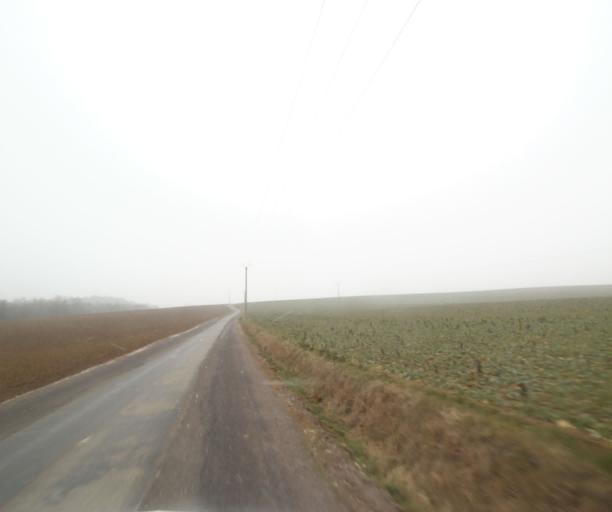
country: FR
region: Champagne-Ardenne
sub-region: Departement de la Haute-Marne
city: Bienville
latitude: 48.5426
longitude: 5.0672
